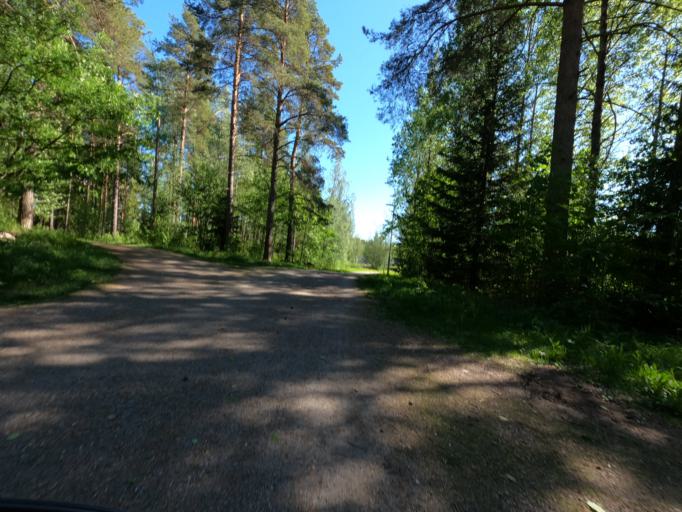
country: FI
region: North Karelia
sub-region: Joensuu
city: Joensuu
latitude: 62.5895
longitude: 29.8000
